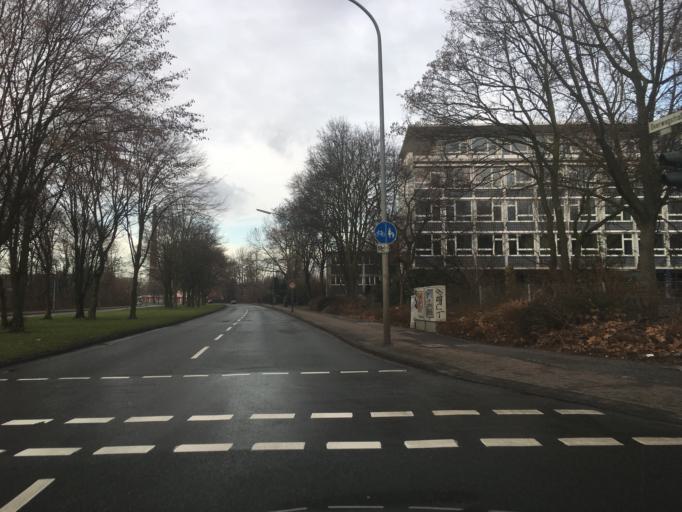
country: DE
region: North Rhine-Westphalia
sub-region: Regierungsbezirk Munster
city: Gelsenkirchen
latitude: 51.5164
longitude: 7.0870
